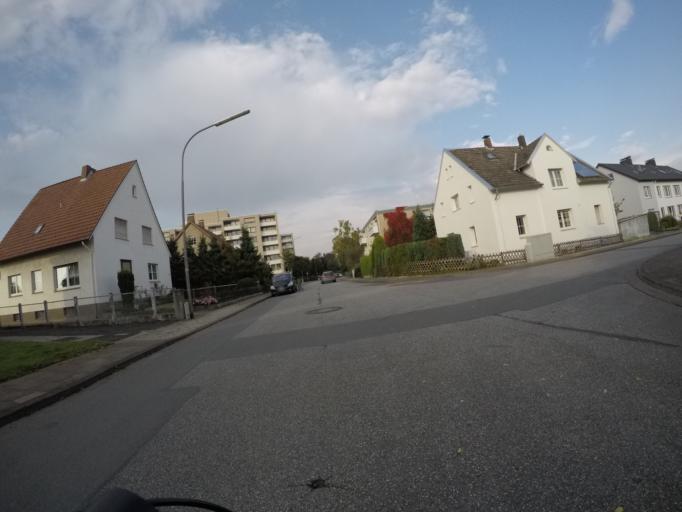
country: DE
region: North Rhine-Westphalia
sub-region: Regierungsbezirk Detmold
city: Herford
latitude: 52.1145
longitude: 8.6468
